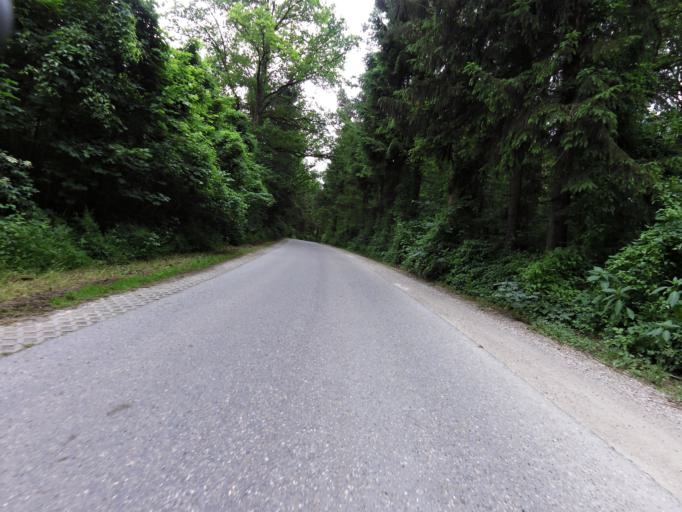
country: DE
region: Bavaria
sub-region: Upper Bavaria
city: Wang
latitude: 48.4912
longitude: 11.9831
